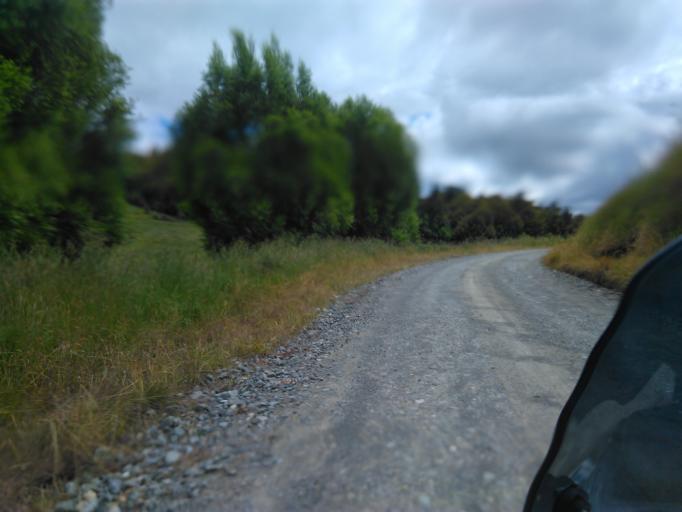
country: NZ
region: Gisborne
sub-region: Gisborne District
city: Gisborne
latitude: -38.1885
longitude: 178.1015
